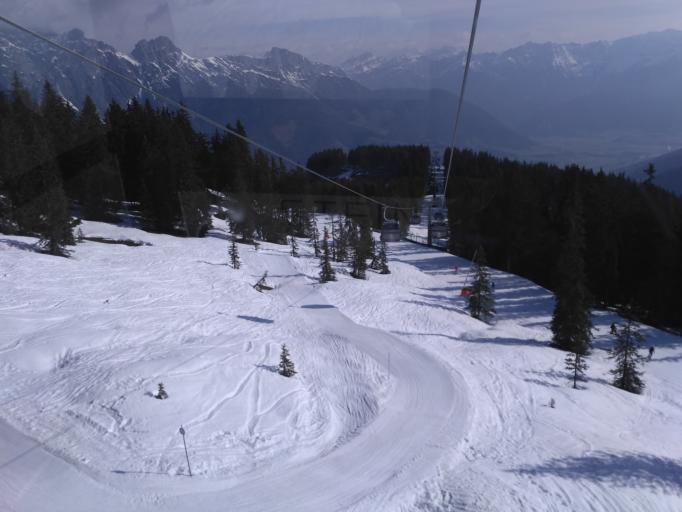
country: AT
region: Salzburg
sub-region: Politischer Bezirk Zell am See
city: Viehhofen
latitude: 47.4125
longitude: 12.7180
